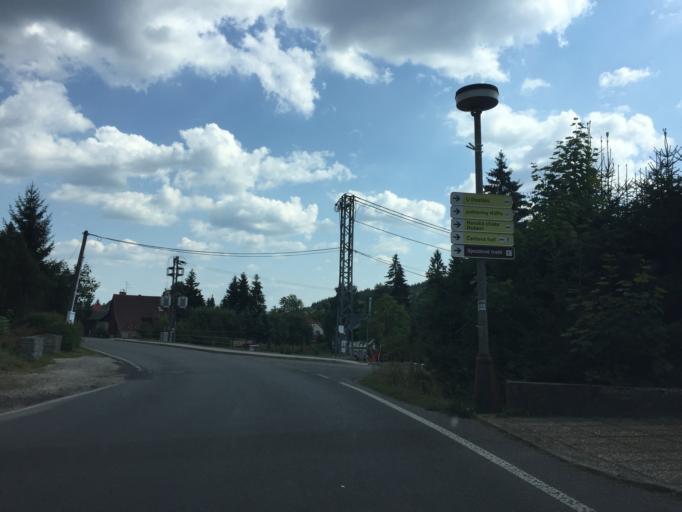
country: CZ
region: Liberecky
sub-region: Okres Jablonec nad Nisou
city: Janov nad Nisou
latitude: 50.7914
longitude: 15.1424
